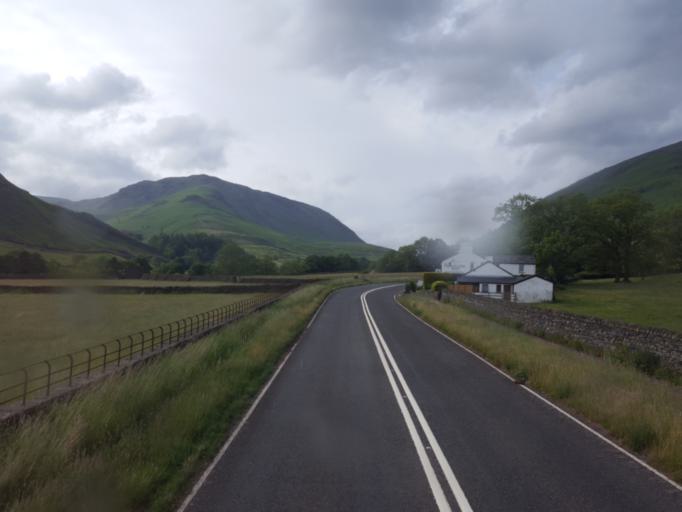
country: GB
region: England
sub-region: Cumbria
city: Ambleside
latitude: 54.4701
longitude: -3.0251
